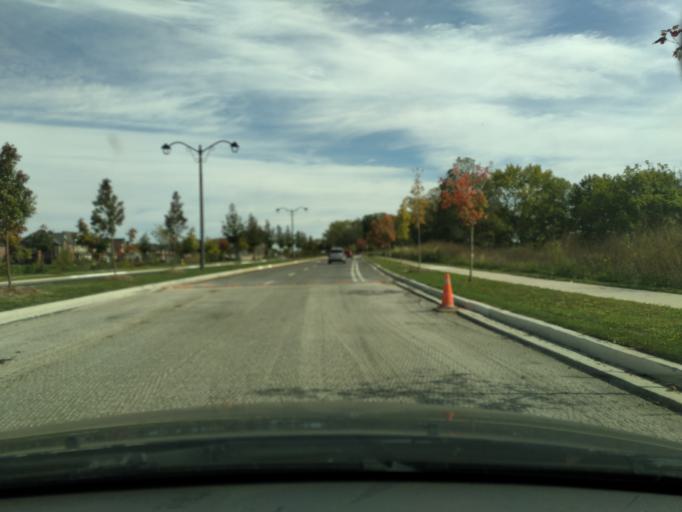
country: CA
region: Ontario
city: Oshawa
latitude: 43.9542
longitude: -78.9085
